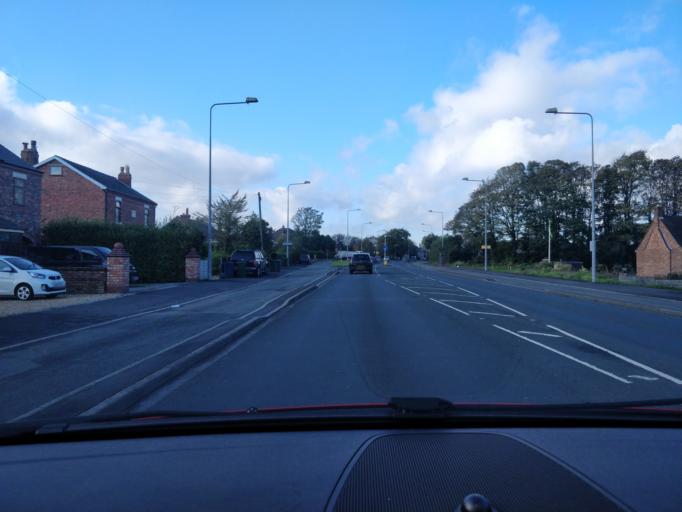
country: GB
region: England
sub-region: Sefton
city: Southport
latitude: 53.6230
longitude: -2.9595
